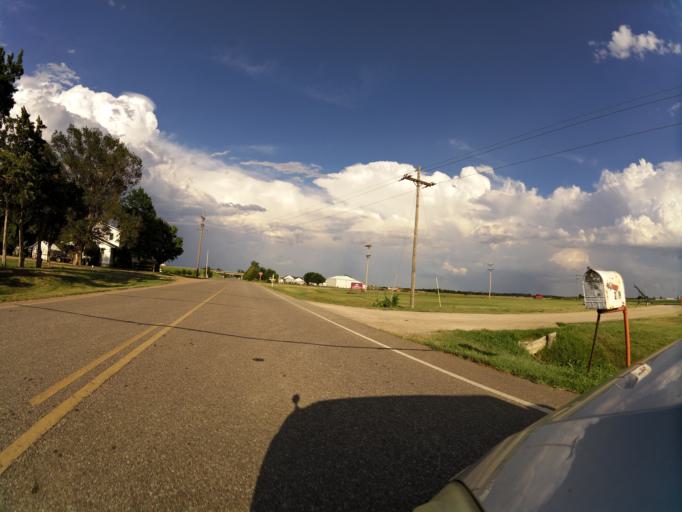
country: US
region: Kansas
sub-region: Reno County
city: South Hutchinson
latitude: 37.9409
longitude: -97.8863
